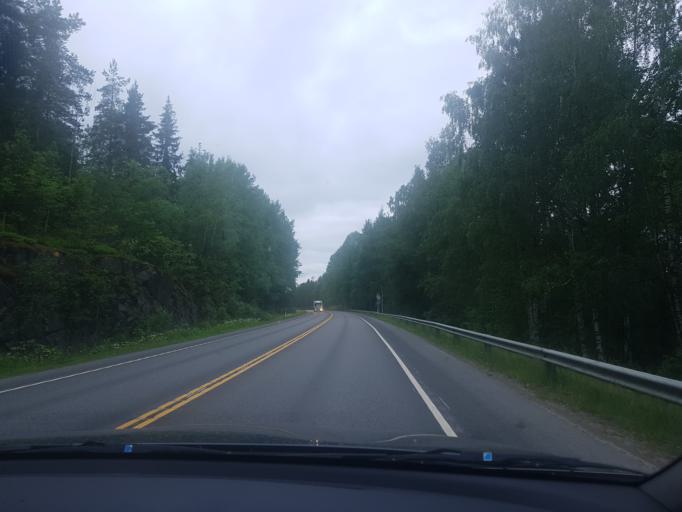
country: FI
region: Pirkanmaa
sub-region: Tampere
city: Paelkaene
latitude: 61.3993
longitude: 24.2053
